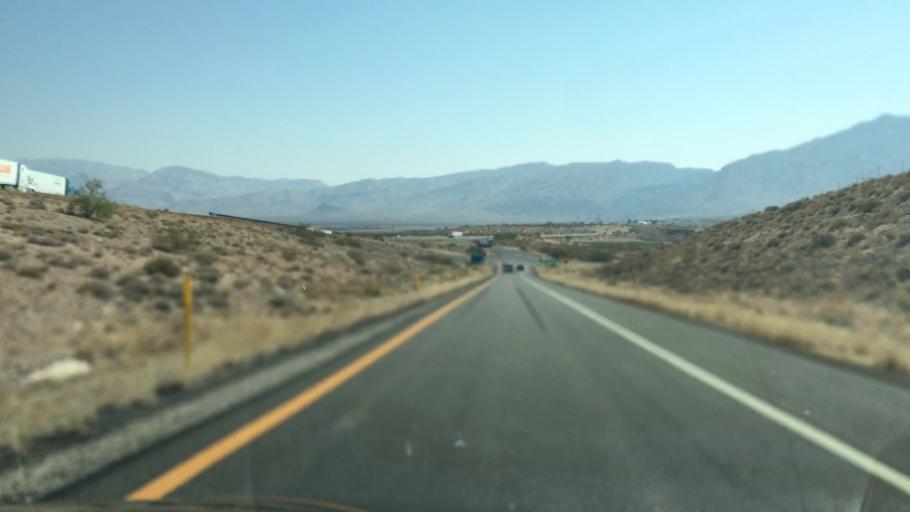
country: US
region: Arizona
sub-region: Mohave County
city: Beaver Dam
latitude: 36.8892
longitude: -113.9318
